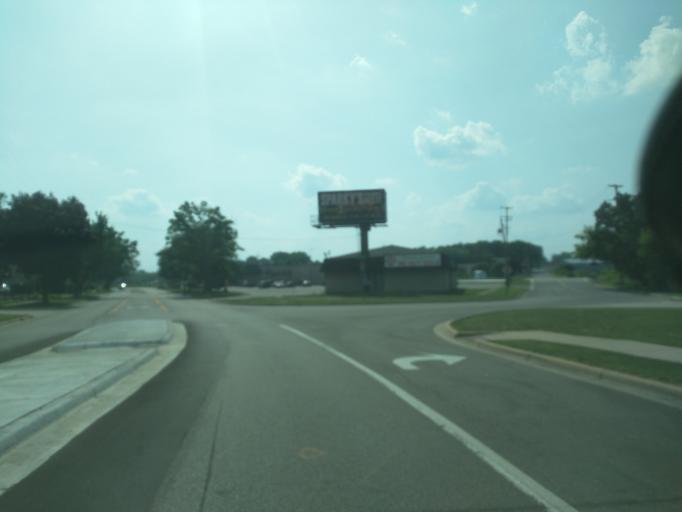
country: US
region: Michigan
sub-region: Jackson County
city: Jackson
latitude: 42.2524
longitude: -84.4308
